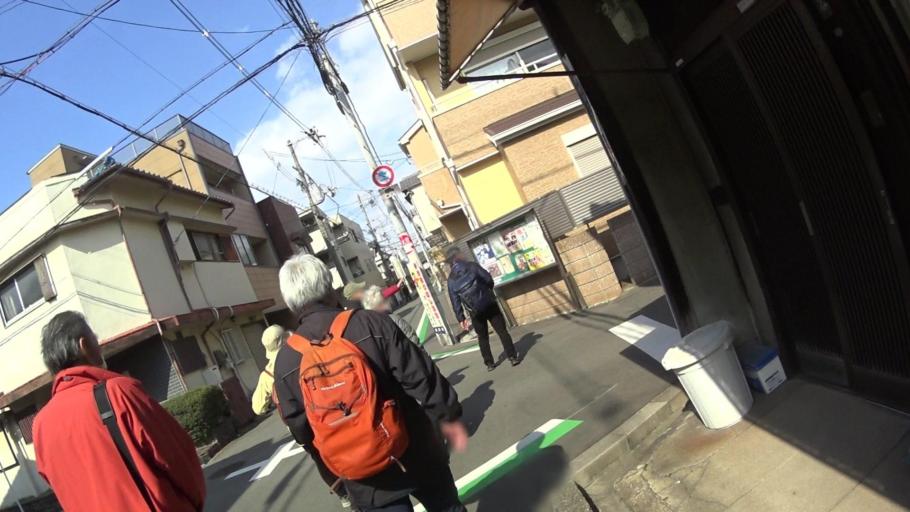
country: JP
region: Osaka
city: Sakai
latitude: 34.6183
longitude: 135.4936
